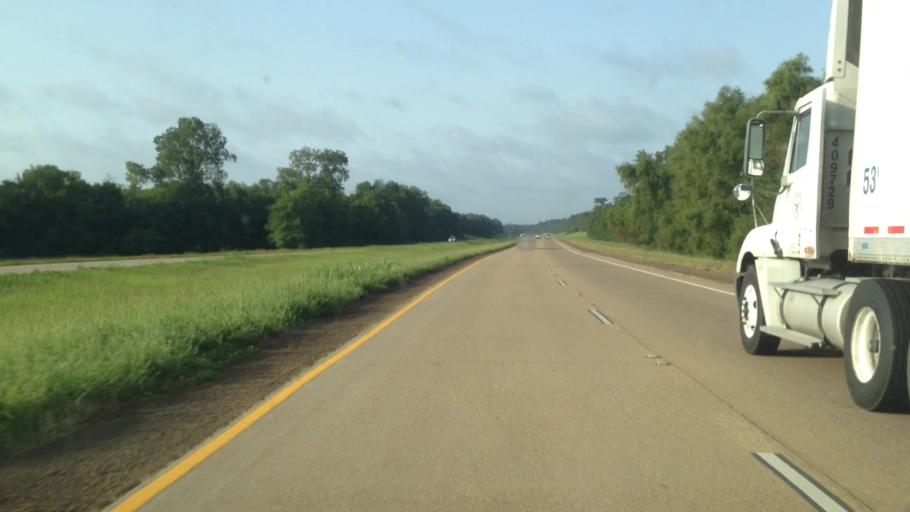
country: US
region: Louisiana
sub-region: Rapides Parish
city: Lecompte
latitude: 31.1192
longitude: -92.4426
